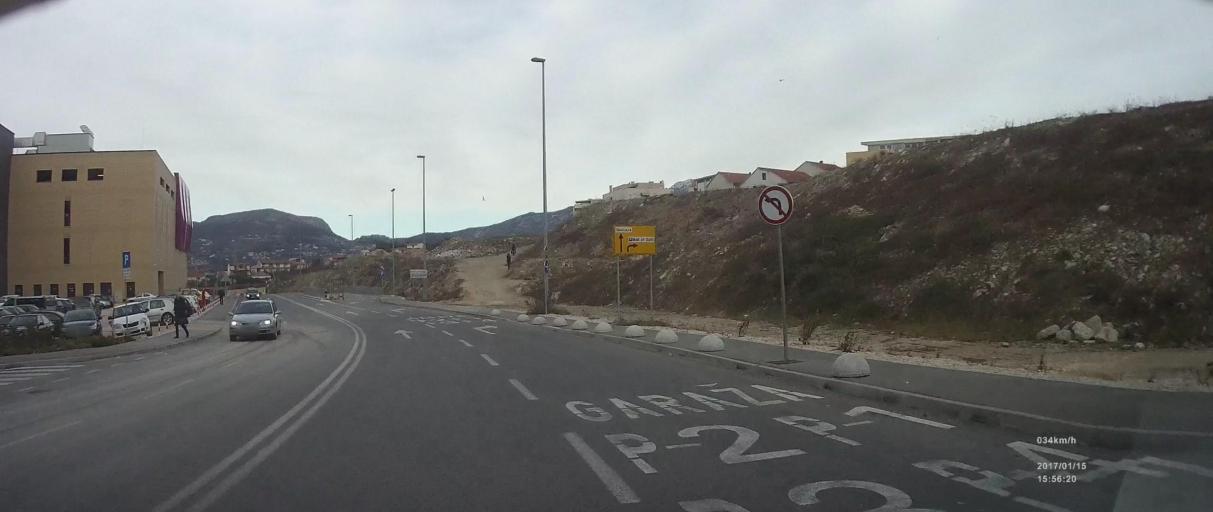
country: HR
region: Splitsko-Dalmatinska
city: Vranjic
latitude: 43.5183
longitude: 16.4849
